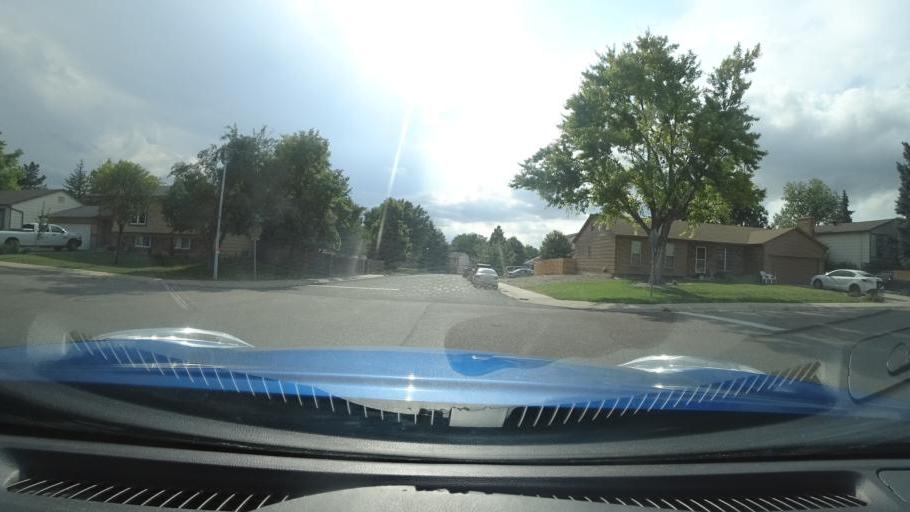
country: US
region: Colorado
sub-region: Adams County
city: Aurora
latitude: 39.6918
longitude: -104.7999
